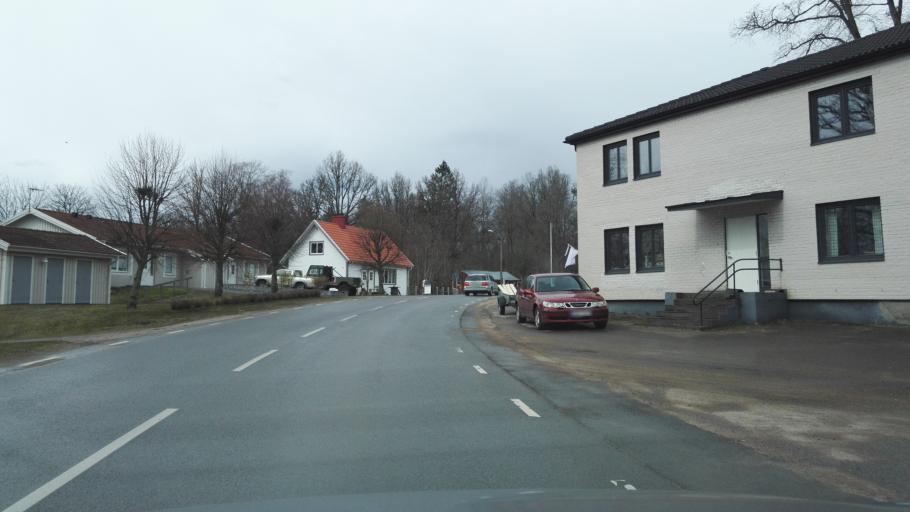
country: SE
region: Joenkoeping
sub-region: Vetlanda Kommun
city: Landsbro
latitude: 57.3080
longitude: 14.8670
